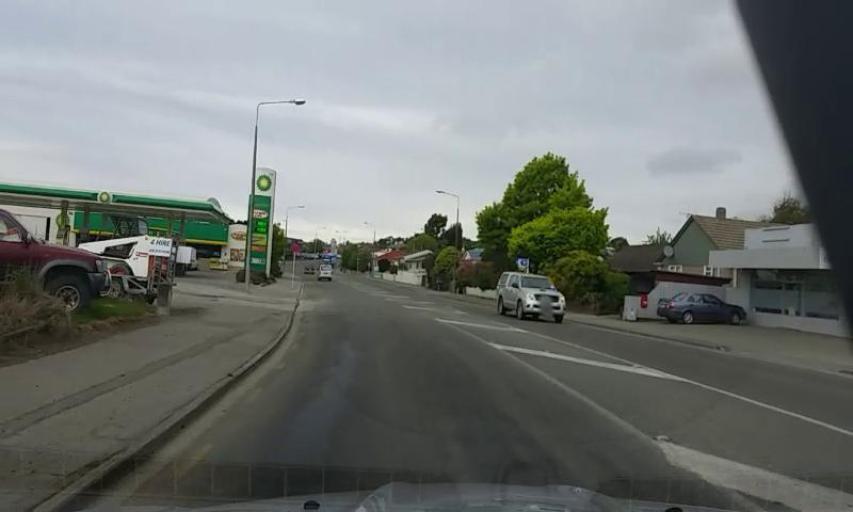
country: NZ
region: Canterbury
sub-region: Timaru District
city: Timaru
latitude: -44.3737
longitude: 171.2415
